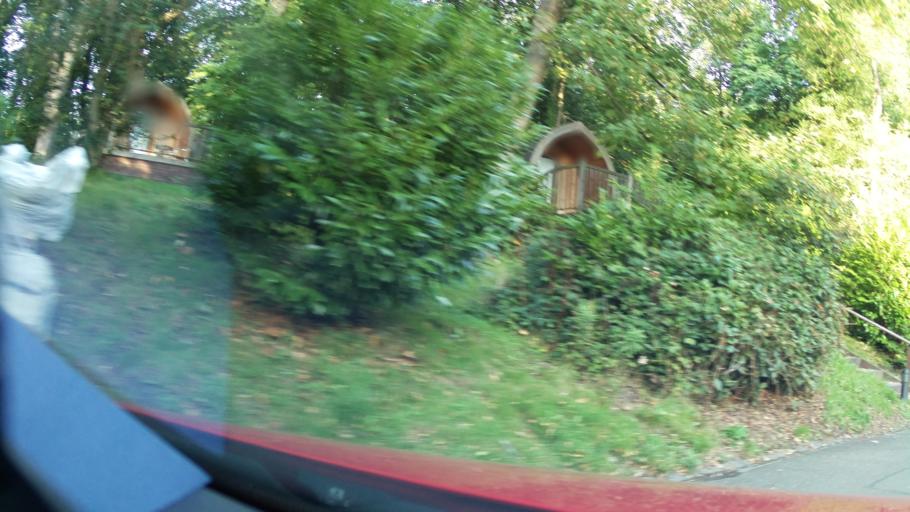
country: GB
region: Scotland
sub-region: Clackmannanshire
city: Alloa
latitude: 56.1265
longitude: -3.8032
